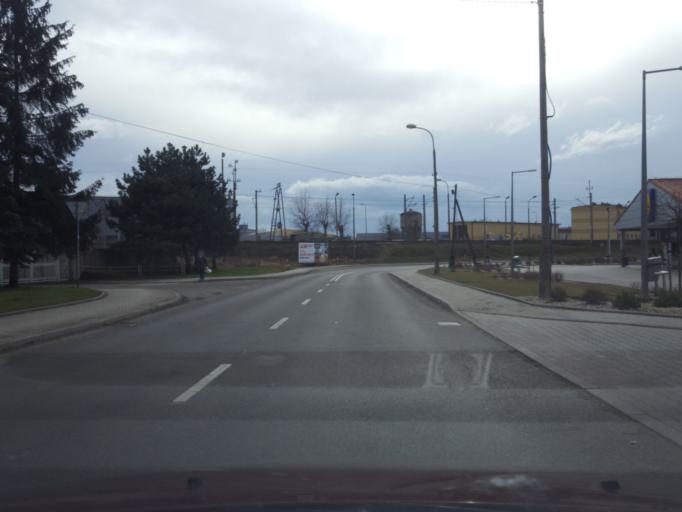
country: PL
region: Lesser Poland Voivodeship
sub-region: Powiat nowosadecki
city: Nowy Sacz
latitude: 49.6091
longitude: 20.7145
